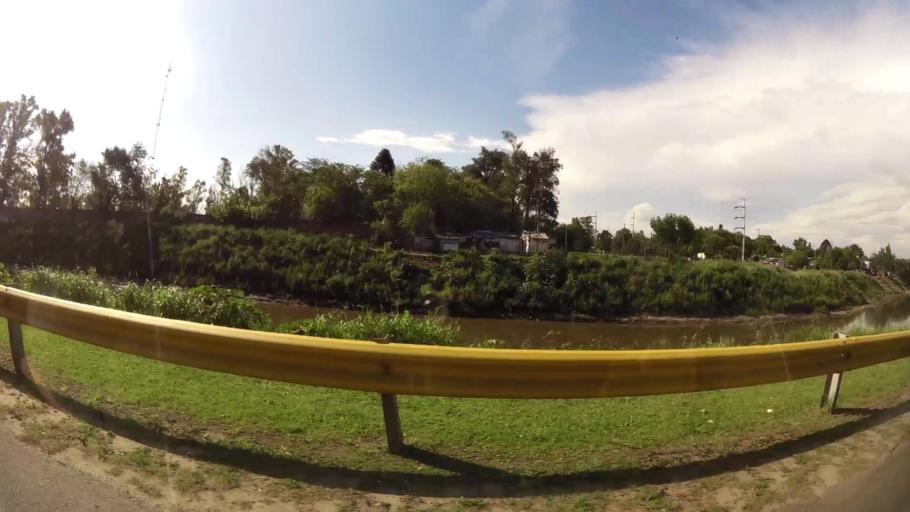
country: AR
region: Buenos Aires
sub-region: Partido de Merlo
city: Merlo
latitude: -34.6549
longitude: -58.7498
